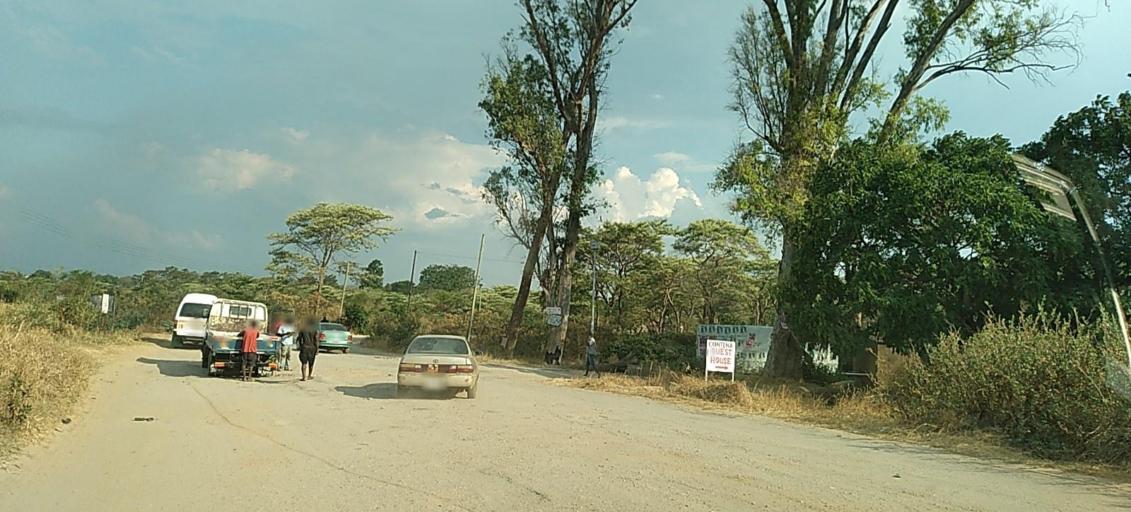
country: ZM
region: Lusaka
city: Lusaka
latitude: -15.5437
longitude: 28.2459
